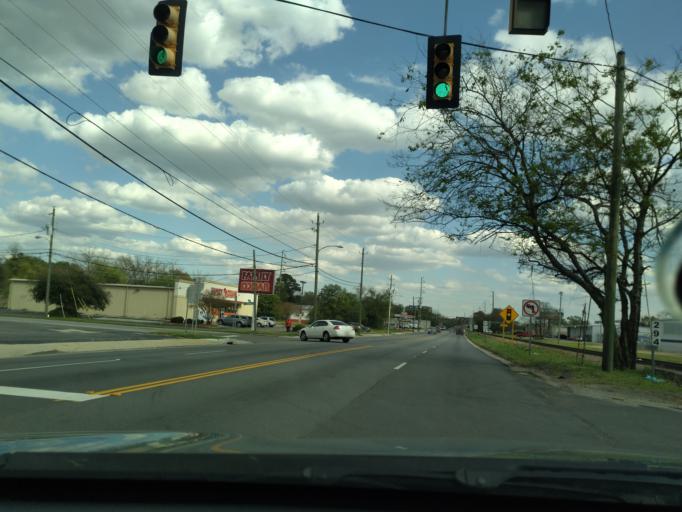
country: US
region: South Carolina
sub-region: Florence County
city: Florence
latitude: 34.2068
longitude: -79.7711
